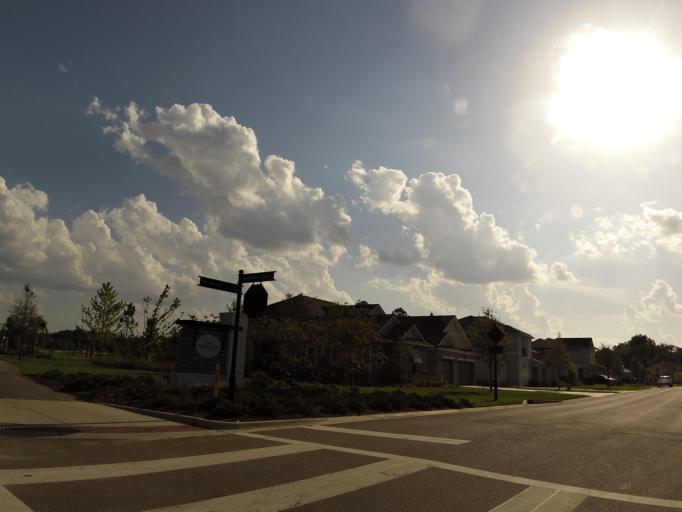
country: US
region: Florida
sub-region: Clay County
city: Green Cove Springs
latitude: 30.0356
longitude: -81.6232
